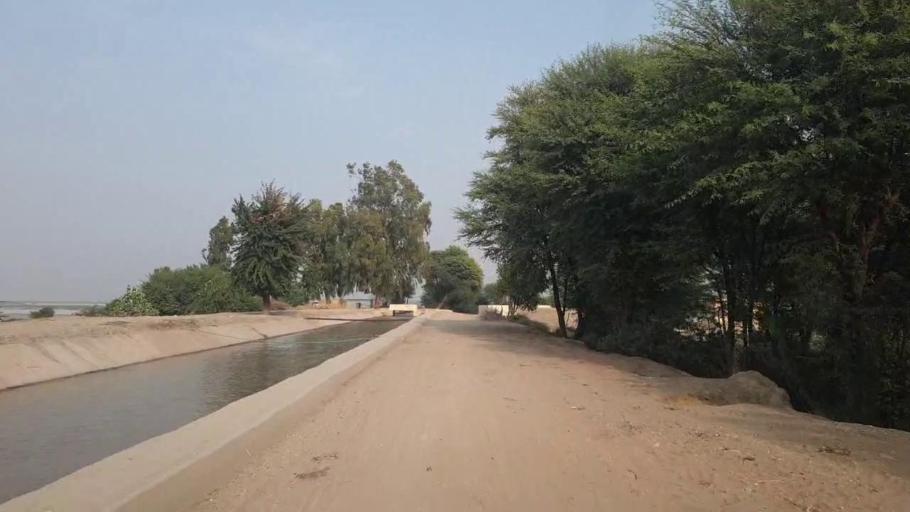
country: PK
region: Sindh
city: Sann
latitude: 26.0703
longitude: 68.1158
